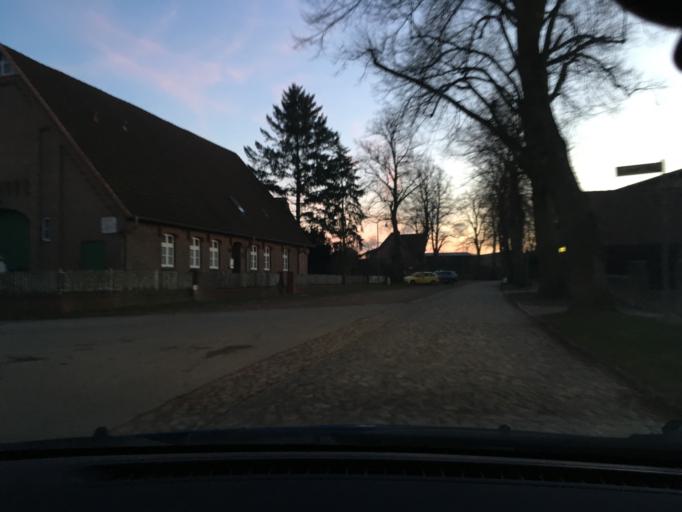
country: DE
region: Schleswig-Holstein
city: Fitzen
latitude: 53.4962
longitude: 10.6481
